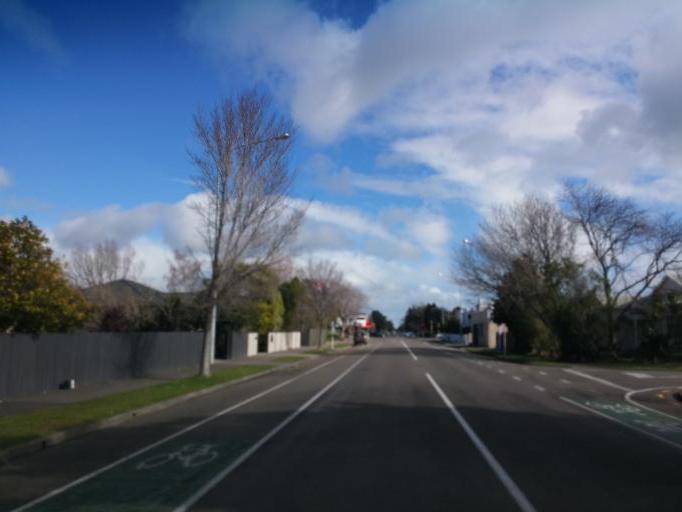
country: NZ
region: Manawatu-Wanganui
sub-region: Palmerston North City
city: Palmerston North
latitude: -40.3615
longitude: 175.6175
